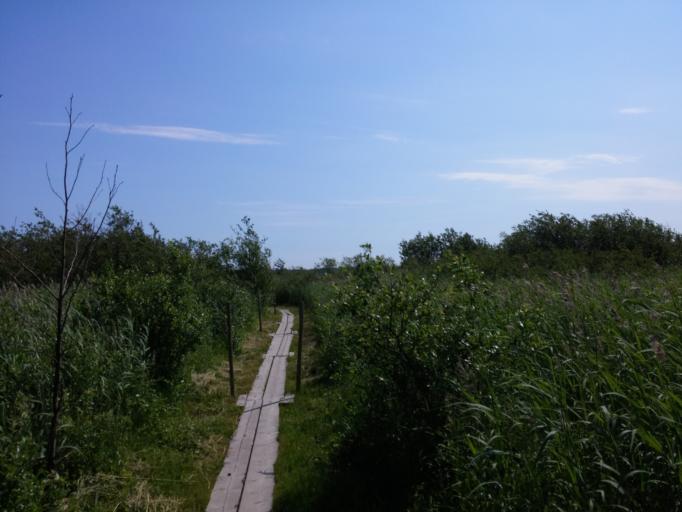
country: FI
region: Uusimaa
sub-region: Helsinki
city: Helsinki
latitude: 60.2130
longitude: 24.9909
